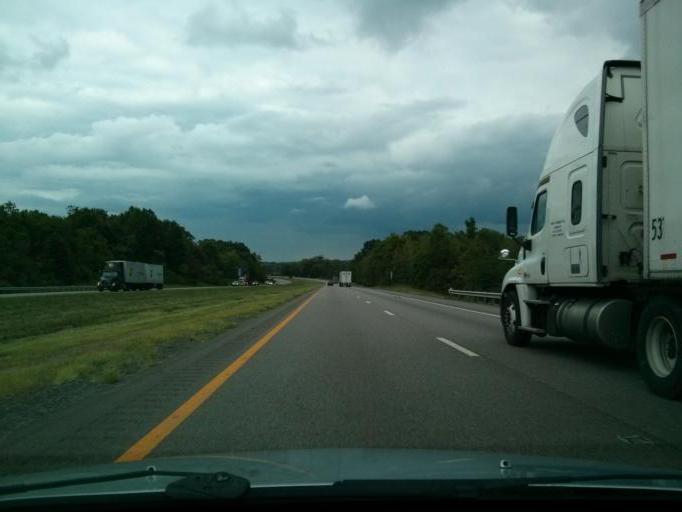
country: US
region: Ohio
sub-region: Trumbull County
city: Churchill
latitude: 41.1590
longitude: -80.6325
